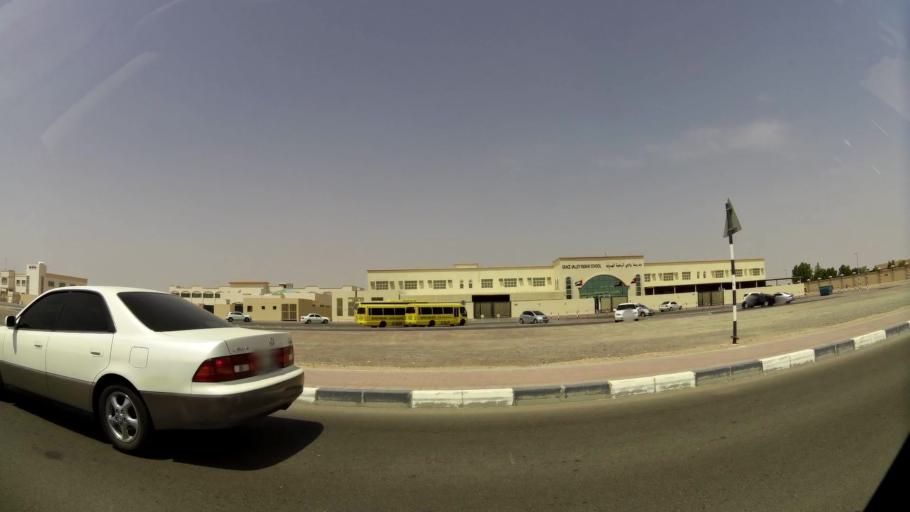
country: AE
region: Abu Dhabi
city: Al Ain
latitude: 24.1869
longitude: 55.7121
